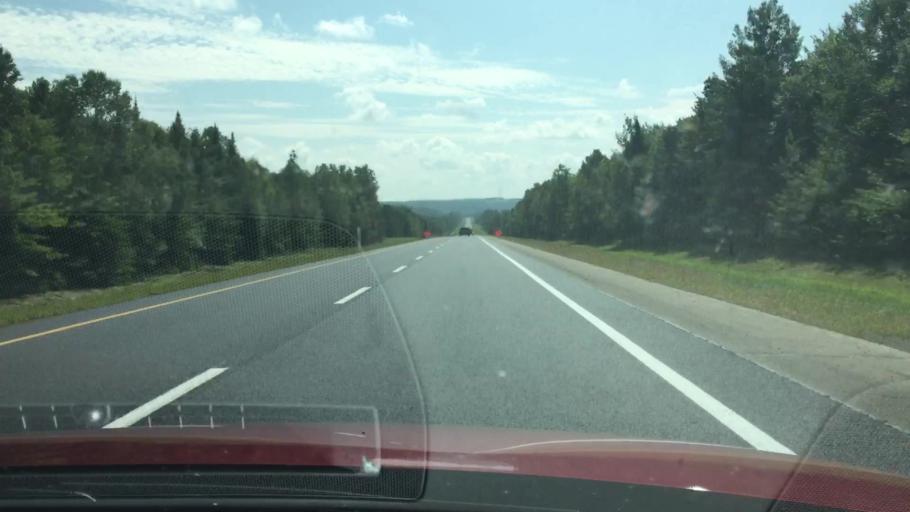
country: US
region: Maine
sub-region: Penobscot County
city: Patten
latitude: 45.8333
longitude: -68.4335
